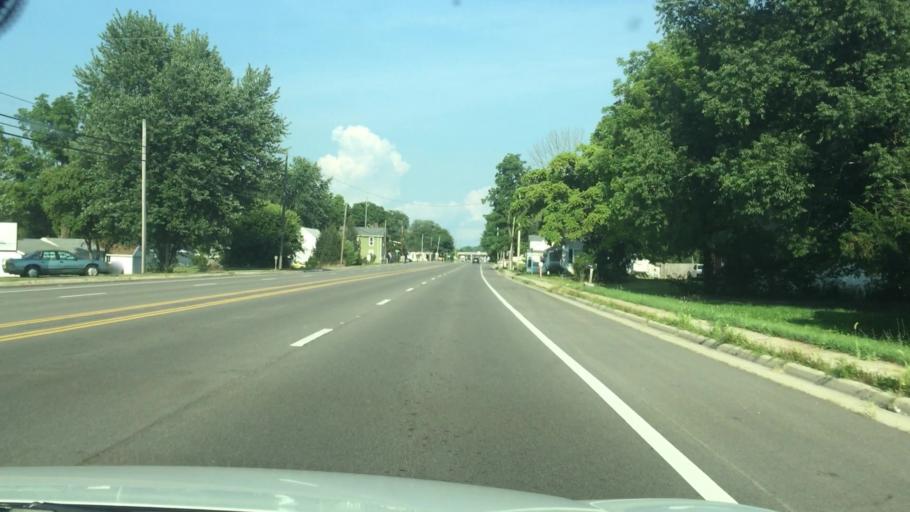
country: US
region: Ohio
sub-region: Clark County
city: Lisbon
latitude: 39.9237
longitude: -83.6994
